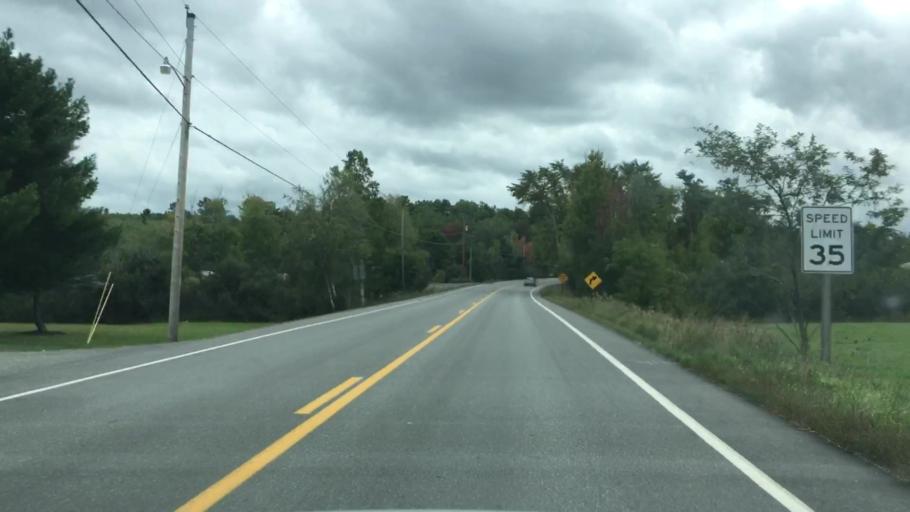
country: US
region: Maine
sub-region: Penobscot County
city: Hermon
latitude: 44.7462
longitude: -68.9672
